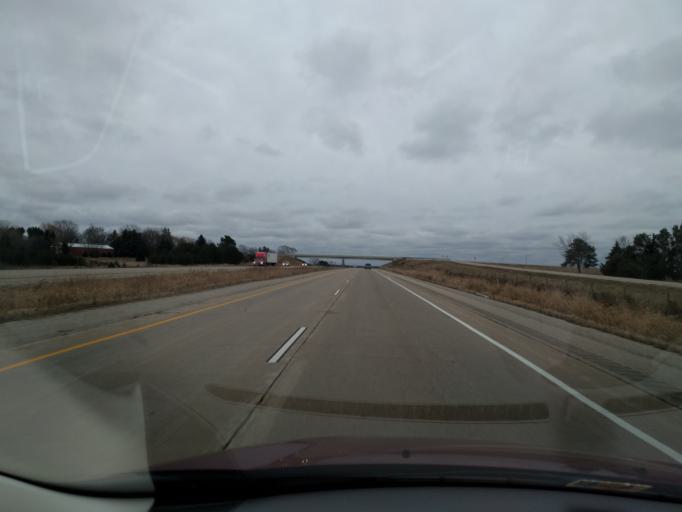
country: US
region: Wisconsin
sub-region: Winnebago County
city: Winneconne
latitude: 44.1865
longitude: -88.6688
